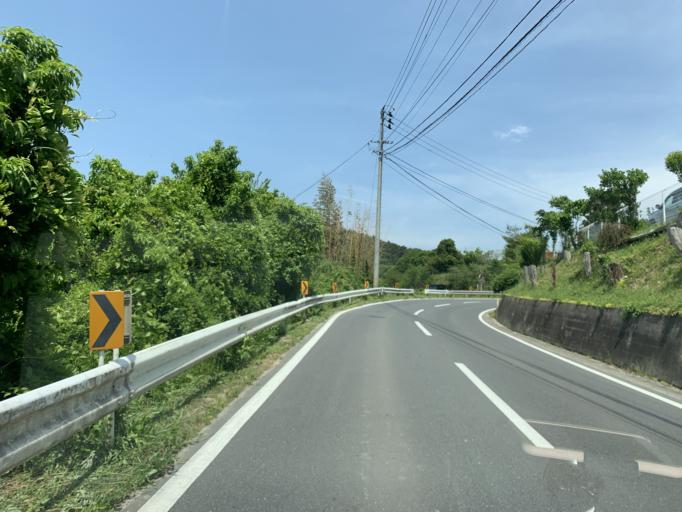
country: JP
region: Iwate
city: Ichinoseki
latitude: 38.9502
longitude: 141.2522
